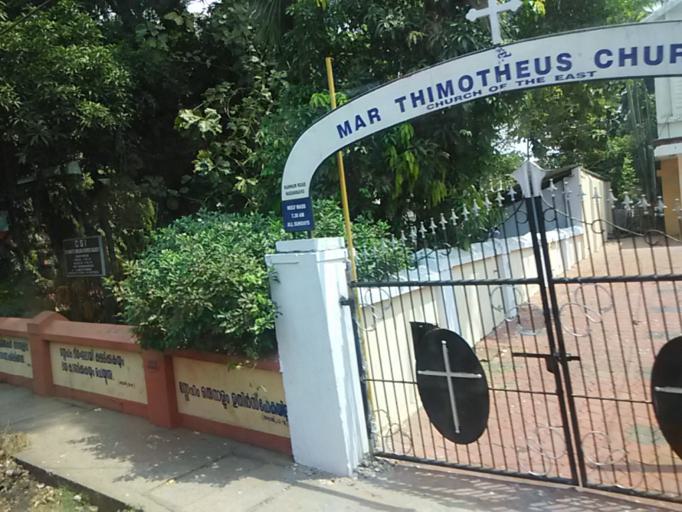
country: IN
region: Kerala
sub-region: Kozhikode
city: Kozhikode
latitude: 11.2682
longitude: 75.7768
